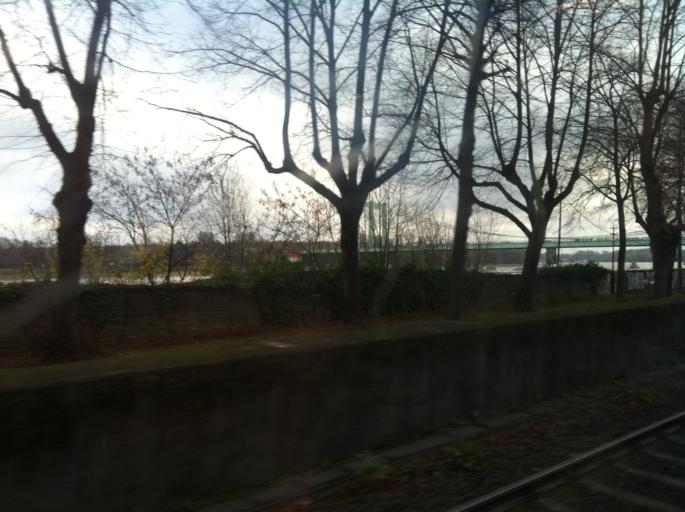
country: DE
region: North Rhine-Westphalia
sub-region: Regierungsbezirk Koln
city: Poll
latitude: 50.9018
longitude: 6.9834
